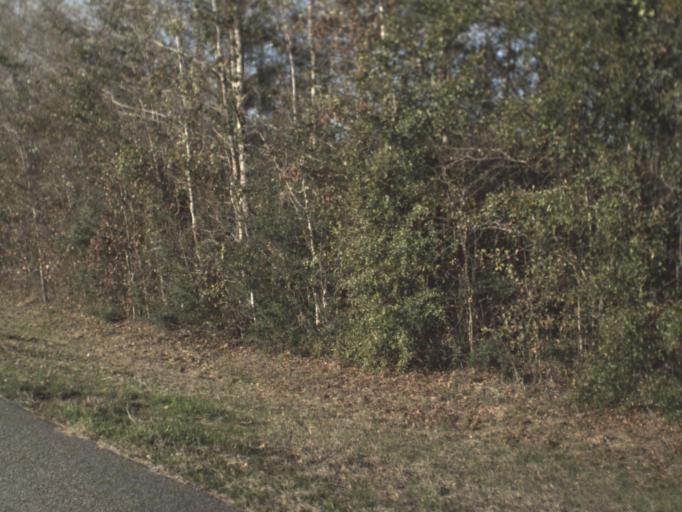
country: US
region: Florida
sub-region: Jackson County
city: Marianna
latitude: 30.6557
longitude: -85.2160
